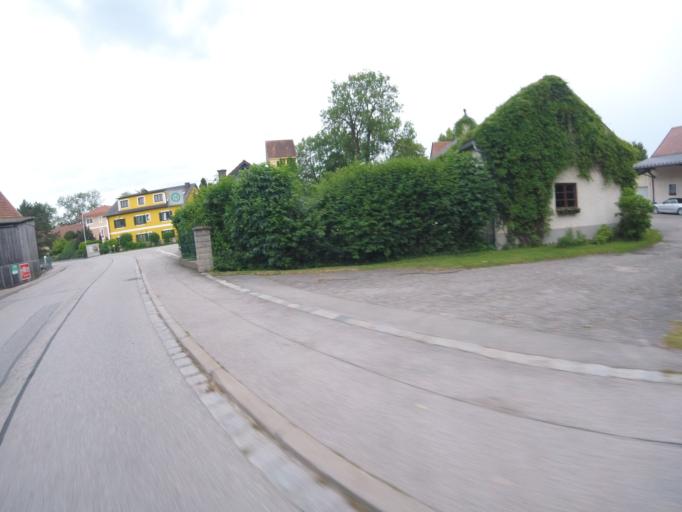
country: DE
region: Bavaria
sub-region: Upper Bavaria
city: Neufahrn bei Freising
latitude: 48.2814
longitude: 11.6726
